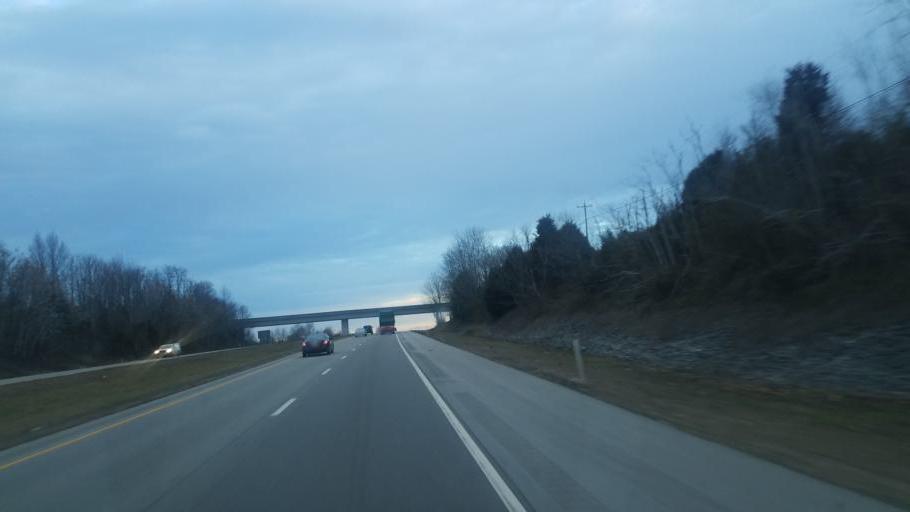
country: US
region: Tennessee
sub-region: Putnam County
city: Cookeville
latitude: 36.0714
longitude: -85.5071
